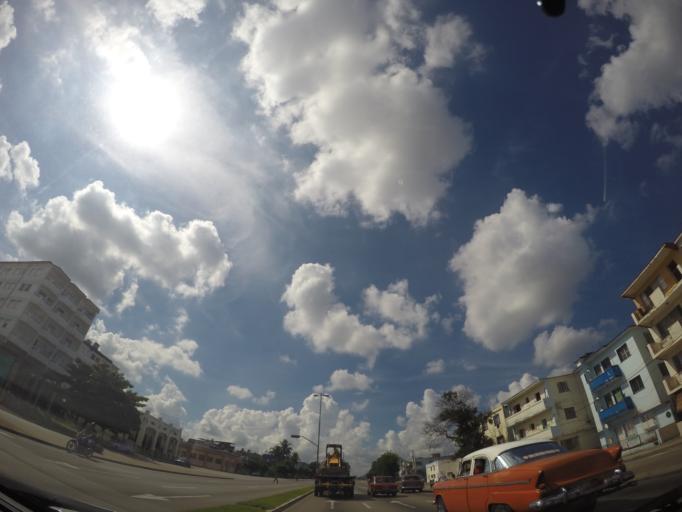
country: CU
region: La Habana
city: Cerro
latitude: 23.1113
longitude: -82.4181
